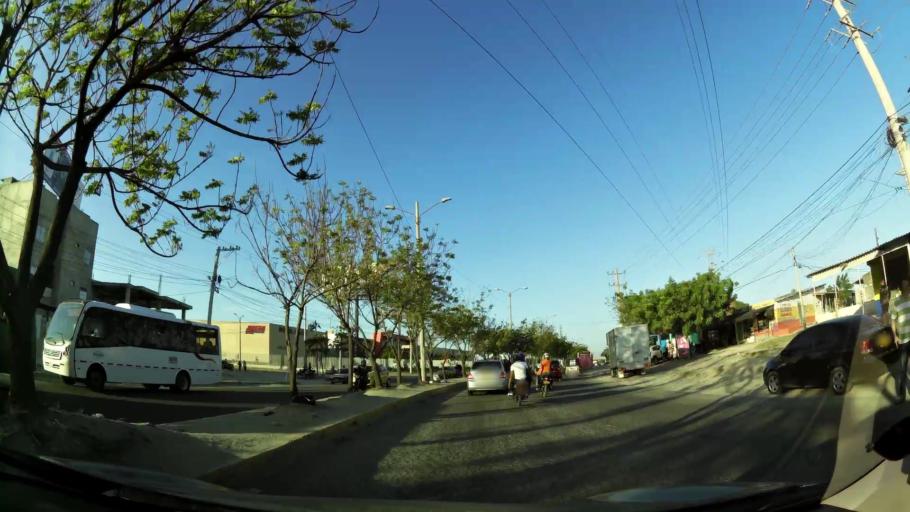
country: CO
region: Atlantico
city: Soledad
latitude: 10.9041
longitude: -74.8020
